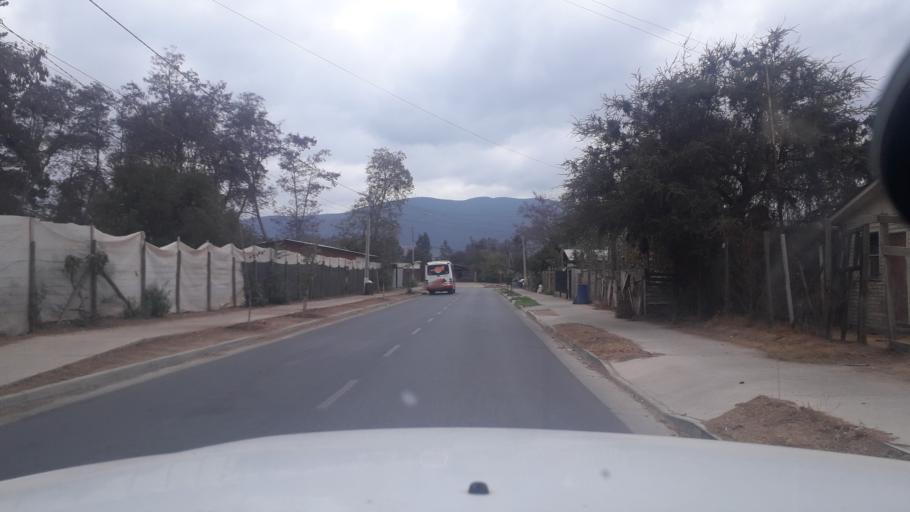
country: CL
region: Valparaiso
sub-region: Provincia de Marga Marga
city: Limache
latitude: -33.0157
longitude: -71.2681
